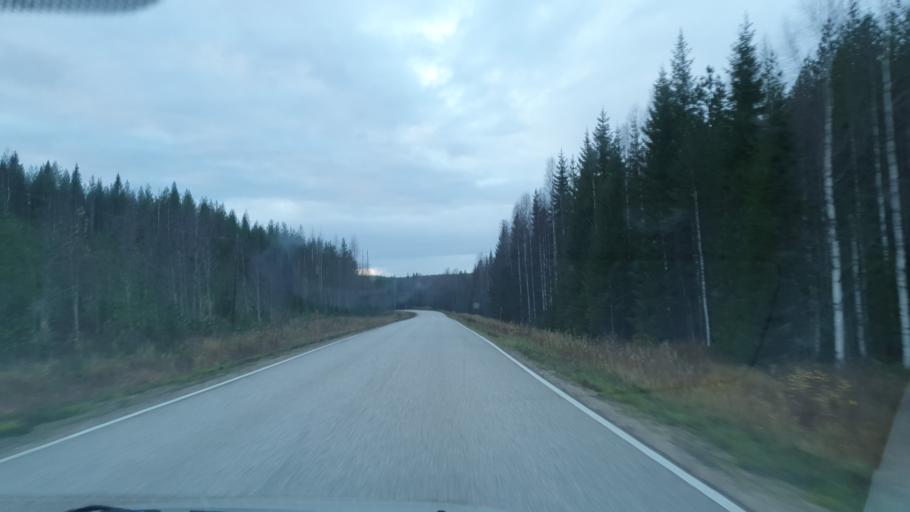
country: FI
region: Kainuu
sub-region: Kajaani
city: Ristijaervi
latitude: 64.4264
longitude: 28.3922
